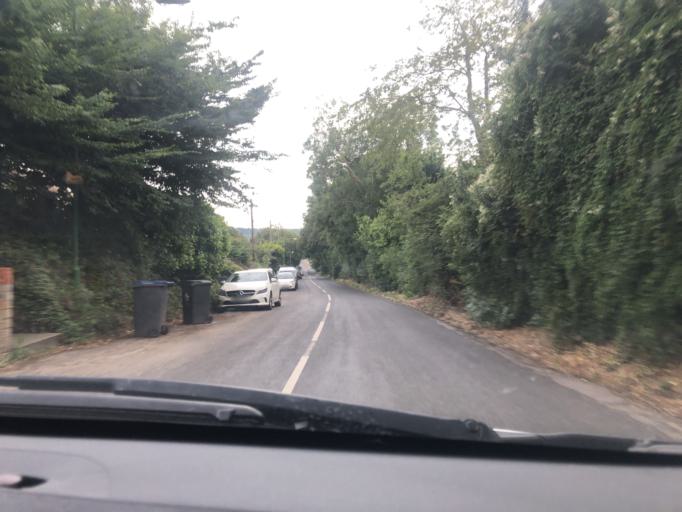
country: GB
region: England
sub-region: Kent
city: Sturry
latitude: 51.3083
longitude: 1.1350
